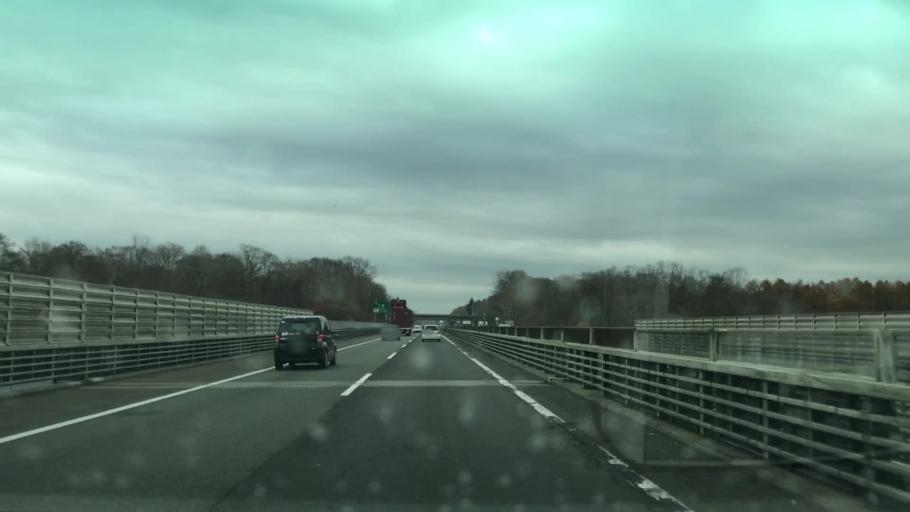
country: JP
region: Hokkaido
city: Chitose
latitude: 42.8165
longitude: 141.6190
